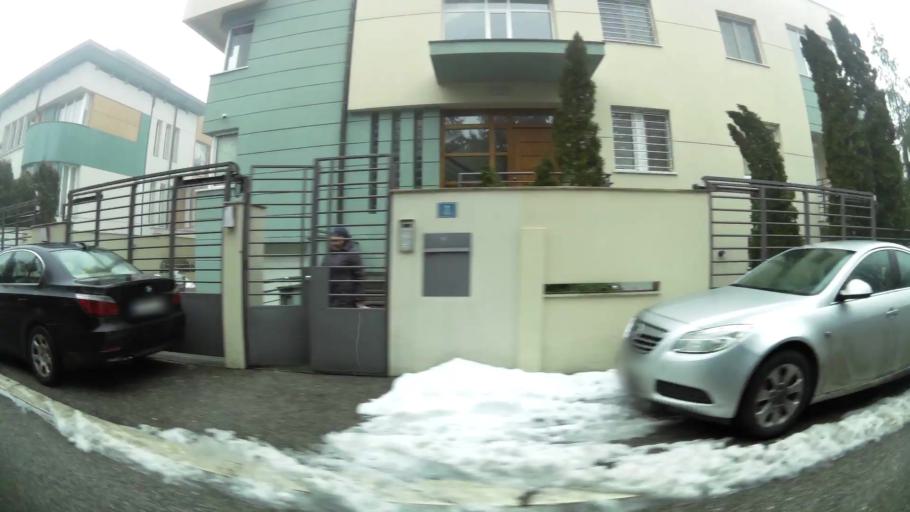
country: RS
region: Central Serbia
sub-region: Belgrade
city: Savski Venac
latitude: 44.7712
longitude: 20.4588
